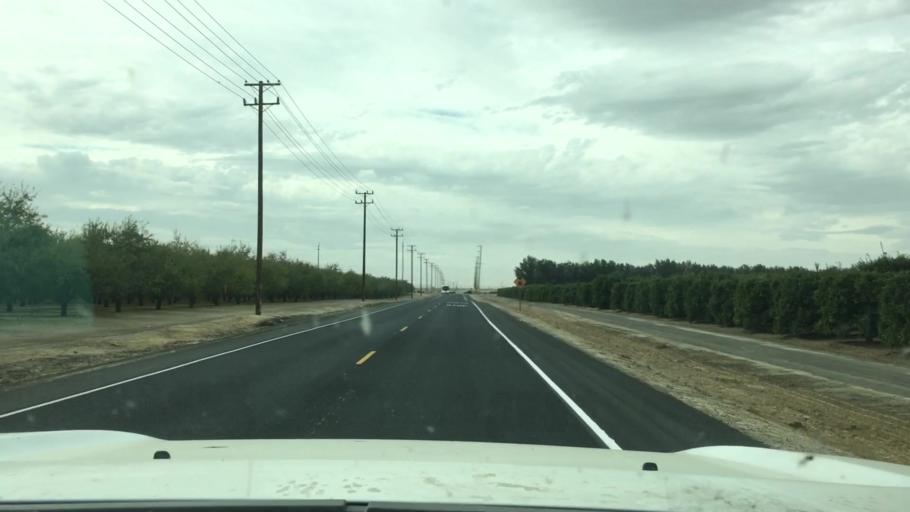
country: US
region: California
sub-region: Kern County
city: Lost Hills
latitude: 35.4991
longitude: -119.7351
